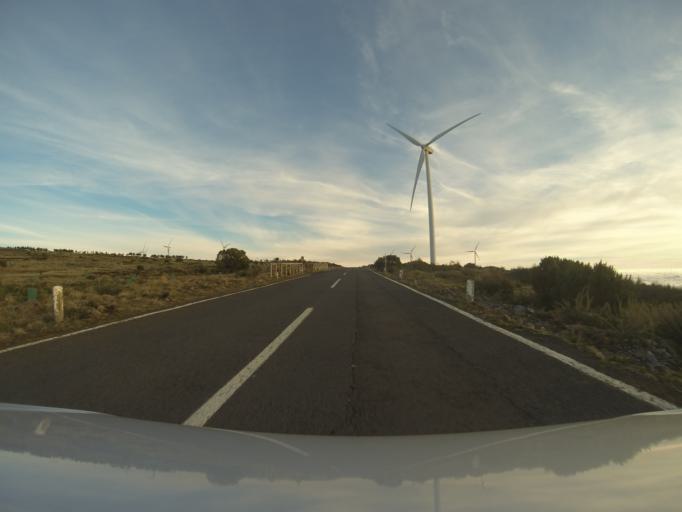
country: PT
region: Madeira
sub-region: Sao Vicente
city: Sao Vicente
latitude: 32.7485
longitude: -17.0579
